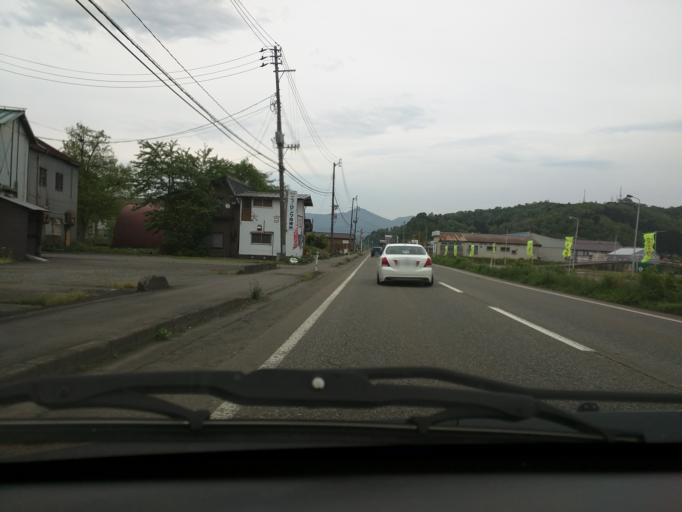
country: JP
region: Niigata
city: Muikamachi
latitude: 37.1922
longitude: 138.9443
